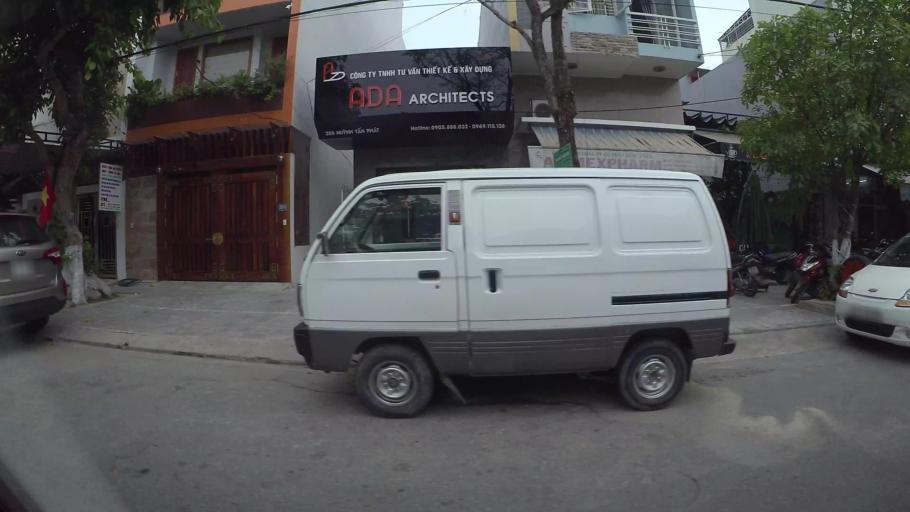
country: VN
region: Da Nang
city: Cam Le
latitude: 16.0333
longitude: 108.2147
